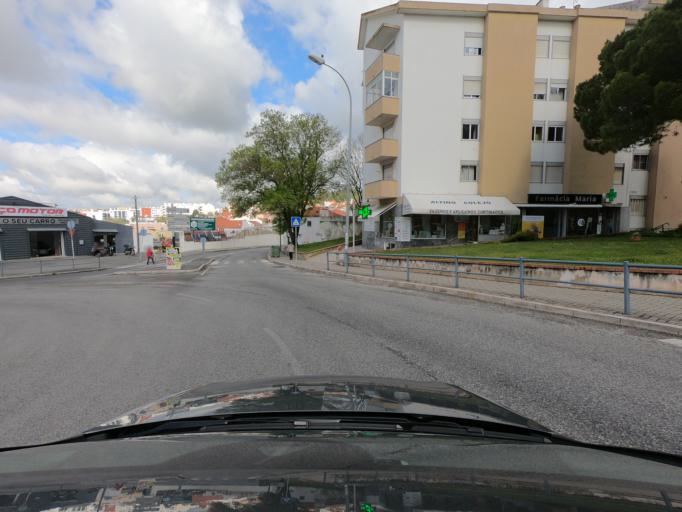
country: PT
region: Lisbon
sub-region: Oeiras
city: Carnaxide
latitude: 38.7245
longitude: -9.2434
